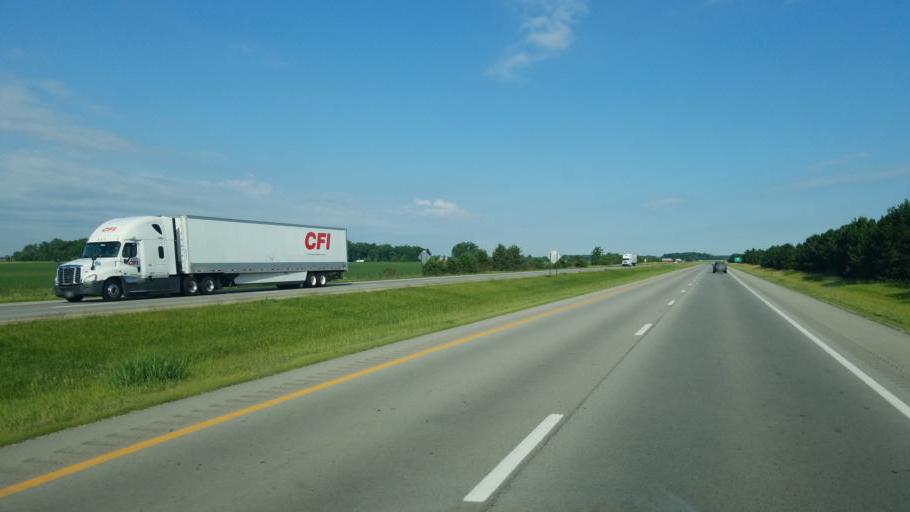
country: US
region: Ohio
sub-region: Wyandot County
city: Carey
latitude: 40.9631
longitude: -83.4684
